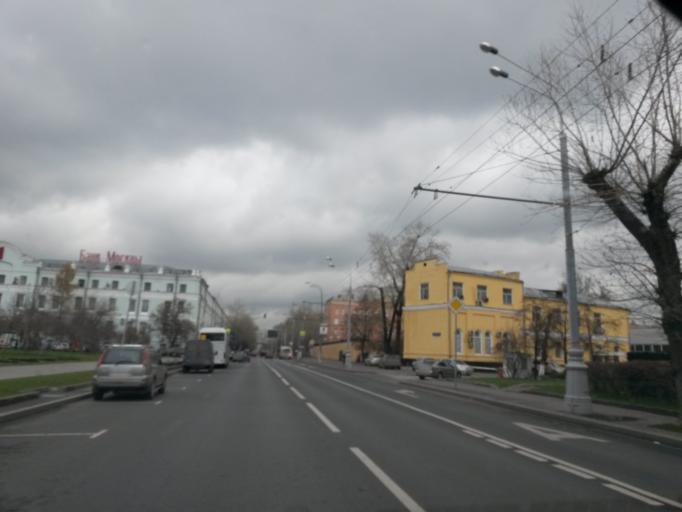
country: RU
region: Moscow
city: Zamoskvorech'ye
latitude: 55.7128
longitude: 37.6235
